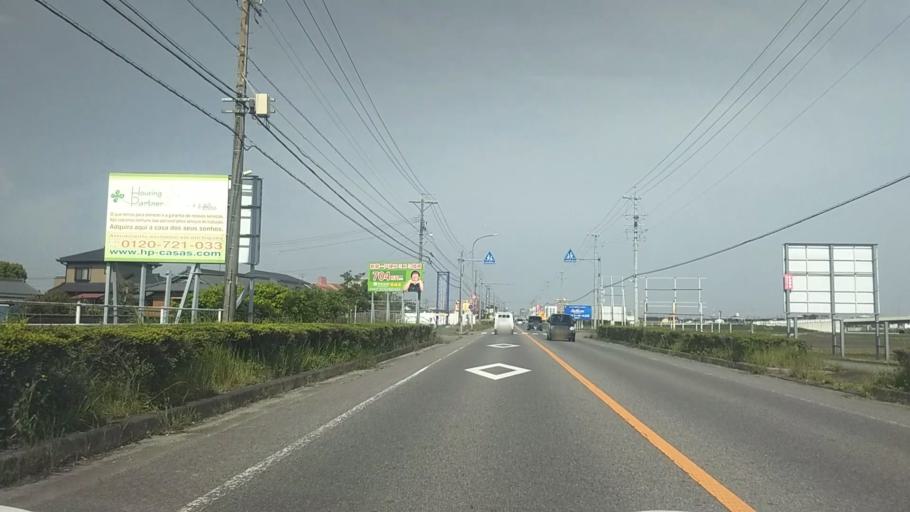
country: JP
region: Aichi
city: Okazaki
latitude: 34.9407
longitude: 137.1346
